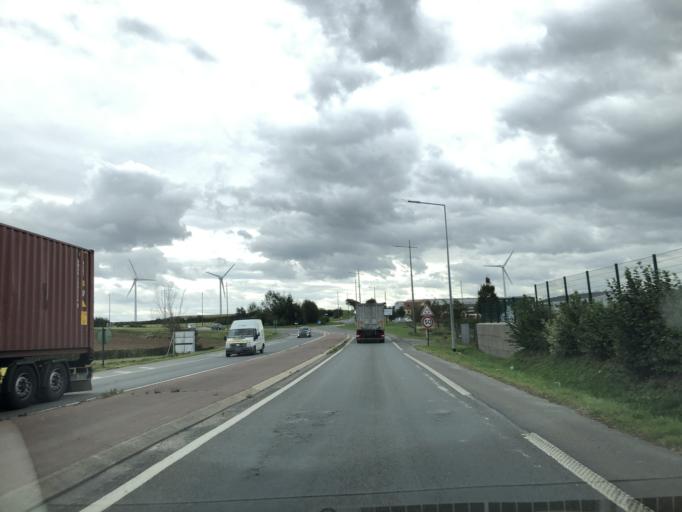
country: FR
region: Nord-Pas-de-Calais
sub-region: Departement du Pas-de-Calais
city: Fruges
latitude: 50.5015
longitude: 2.1300
